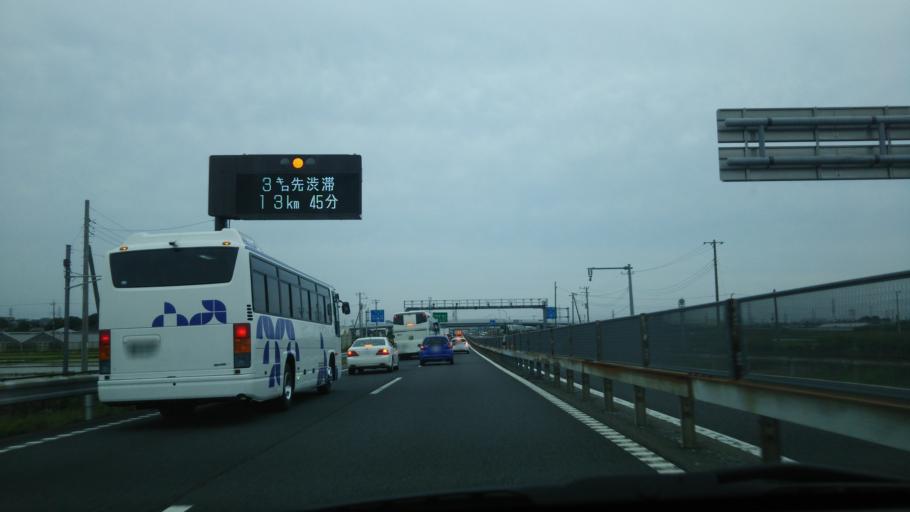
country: JP
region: Kanagawa
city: Isehara
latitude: 35.3822
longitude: 139.3298
